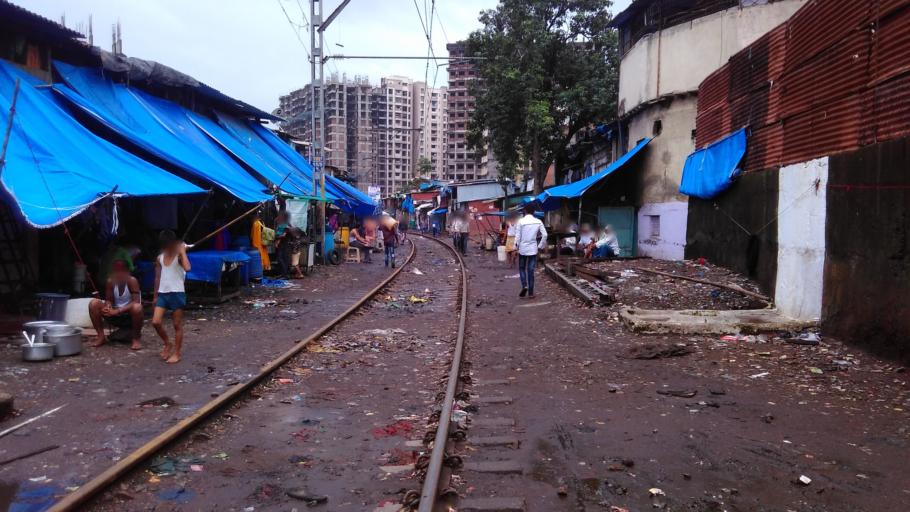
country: IN
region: Maharashtra
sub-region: Mumbai Suburban
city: Mumbai
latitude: 19.0632
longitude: 72.8793
